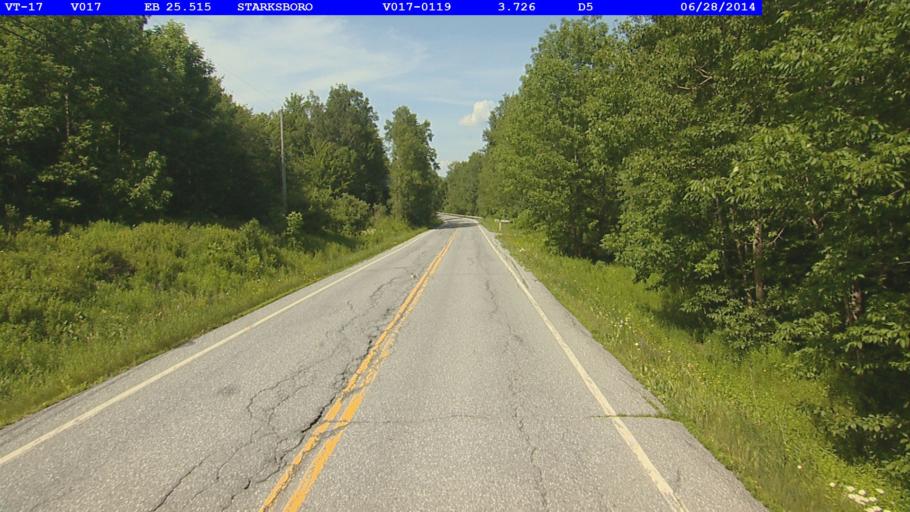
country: US
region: Vermont
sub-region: Addison County
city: Bristol
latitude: 44.1929
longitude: -72.9666
